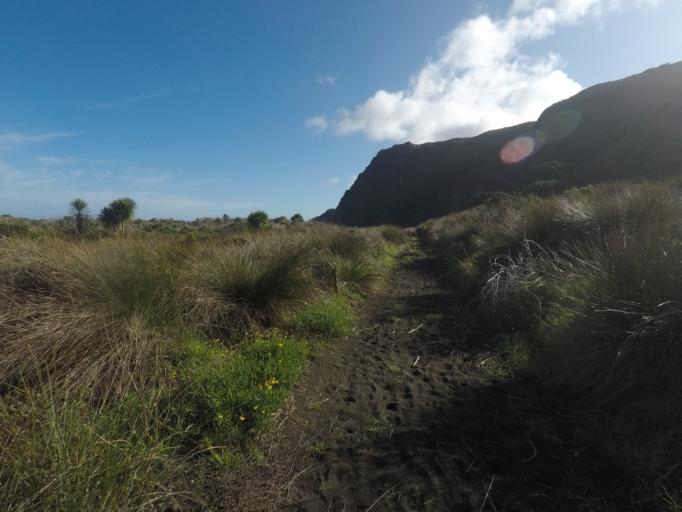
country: NZ
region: Auckland
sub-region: Auckland
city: Titirangi
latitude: -37.0053
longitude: 174.4796
